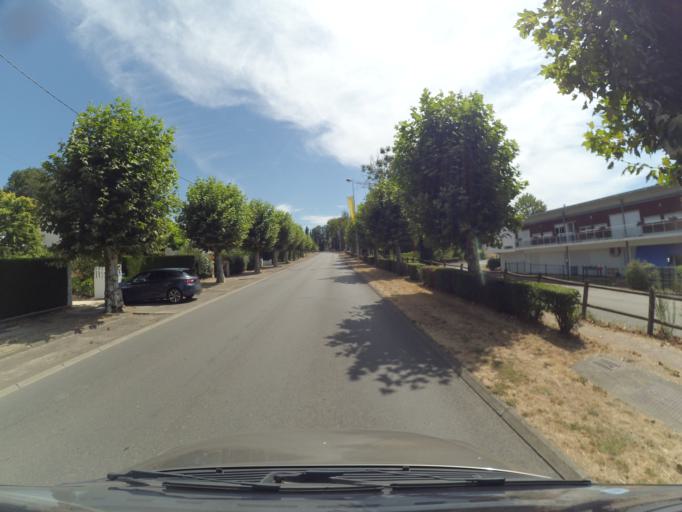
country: FR
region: Poitou-Charentes
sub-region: Departement de la Charente
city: Confolens
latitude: 46.0071
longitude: 0.6724
